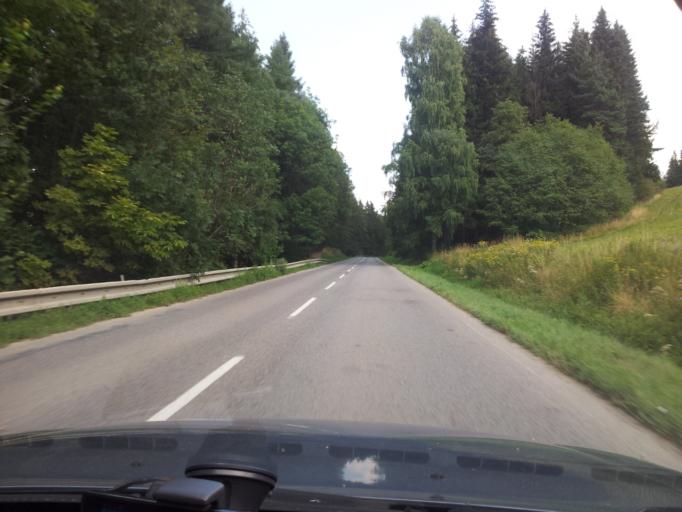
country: SK
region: Zilinsky
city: Namestovo
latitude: 49.3998
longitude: 19.4968
